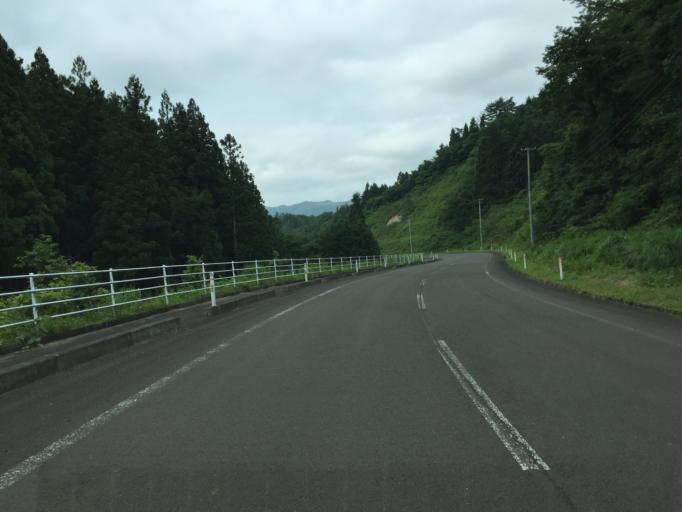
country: JP
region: Miyagi
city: Marumori
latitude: 37.8148
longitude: 140.7339
